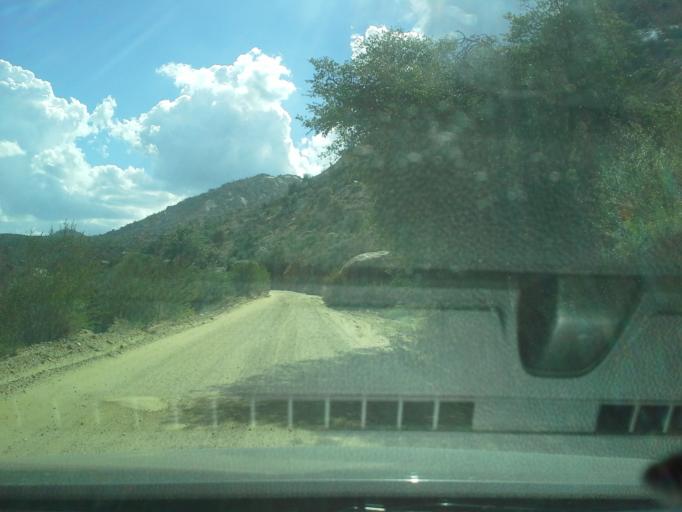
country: US
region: Arizona
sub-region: Yavapai County
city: Mayer
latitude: 34.2306
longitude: -112.3078
